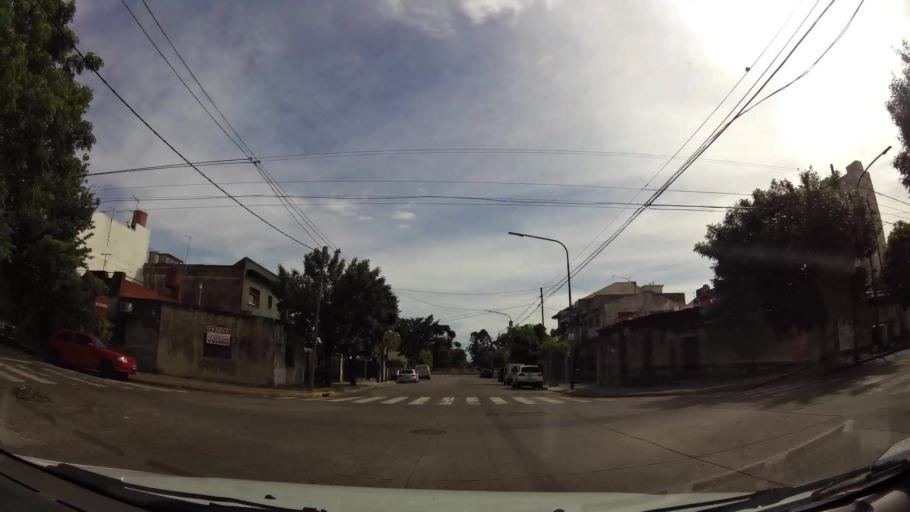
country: AR
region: Buenos Aires F.D.
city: Villa Lugano
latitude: -34.6662
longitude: -58.5104
